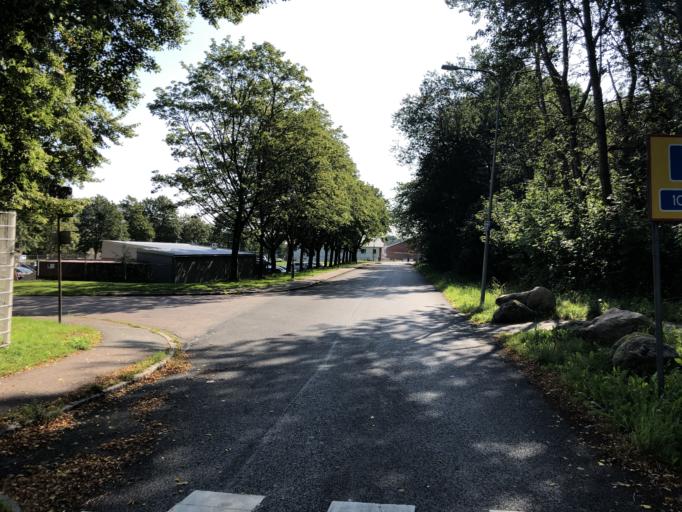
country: SE
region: Vaestra Goetaland
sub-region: Goteborg
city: Goeteborg
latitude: 57.7435
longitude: 11.9647
